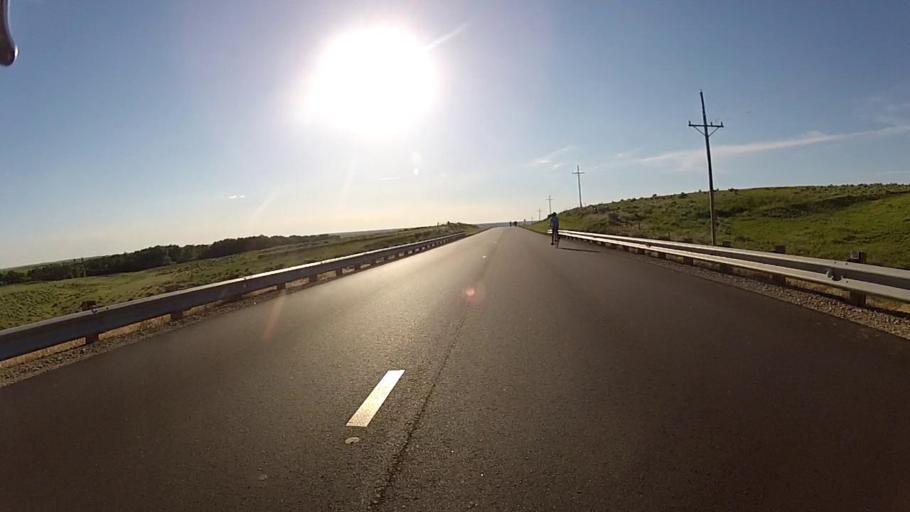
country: US
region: Kansas
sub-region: Comanche County
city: Coldwater
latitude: 37.2819
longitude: -99.0944
